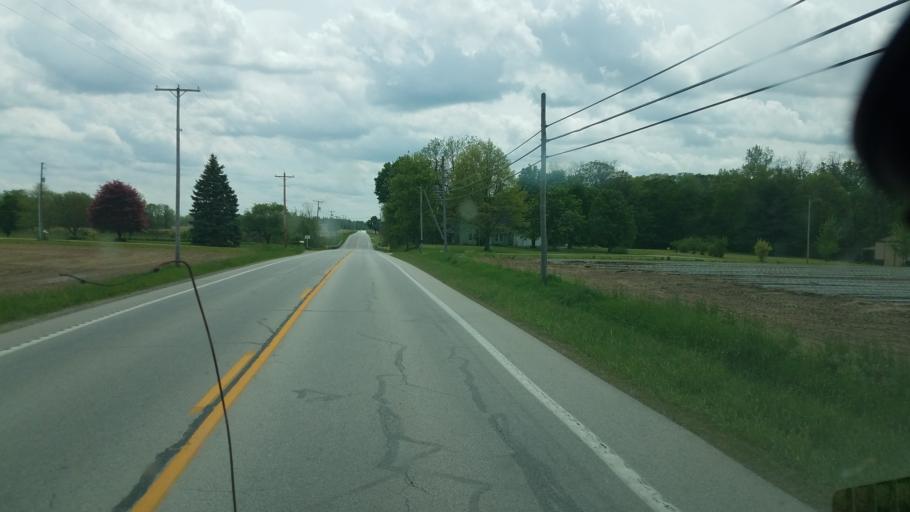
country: US
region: Ohio
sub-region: Seneca County
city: Tiffin
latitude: 41.1759
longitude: -83.1686
